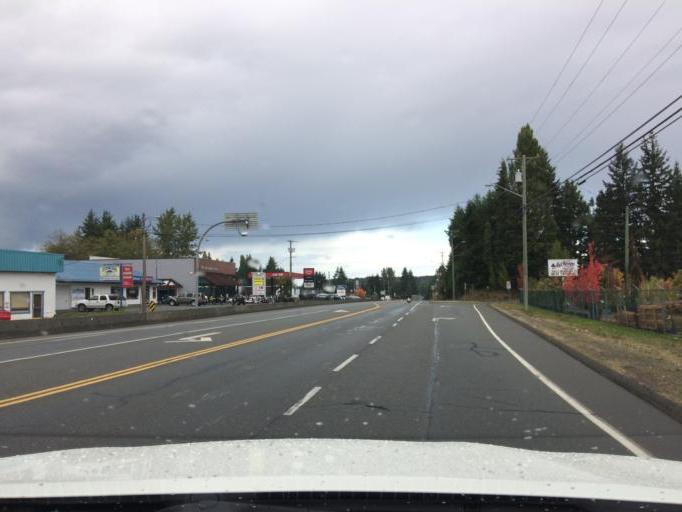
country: CA
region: British Columbia
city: Courtenay
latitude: 49.7153
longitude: -124.9931
